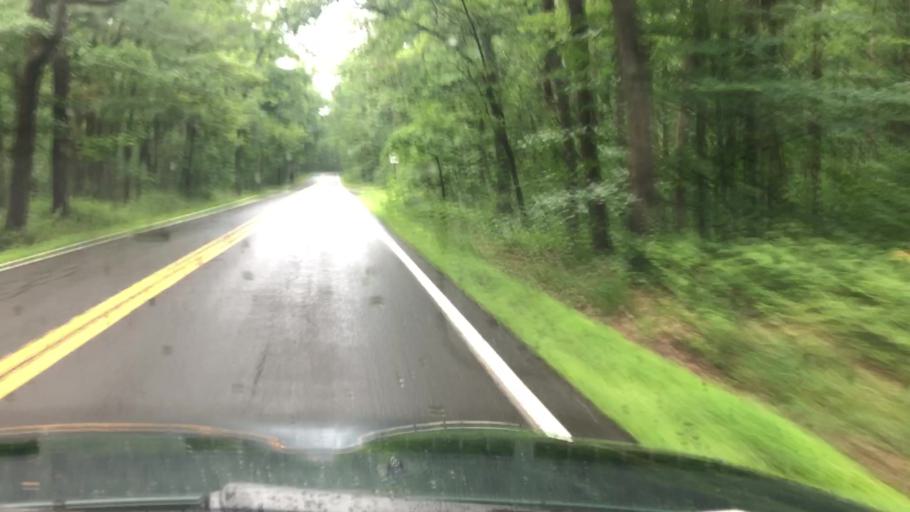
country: US
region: Pennsylvania
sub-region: Wayne County
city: Hawley
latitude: 41.3528
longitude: -75.2105
